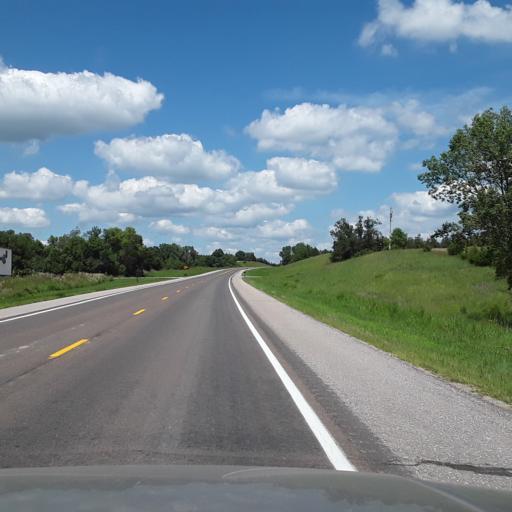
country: US
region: Nebraska
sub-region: Nance County
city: Genoa
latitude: 41.4577
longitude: -97.7250
